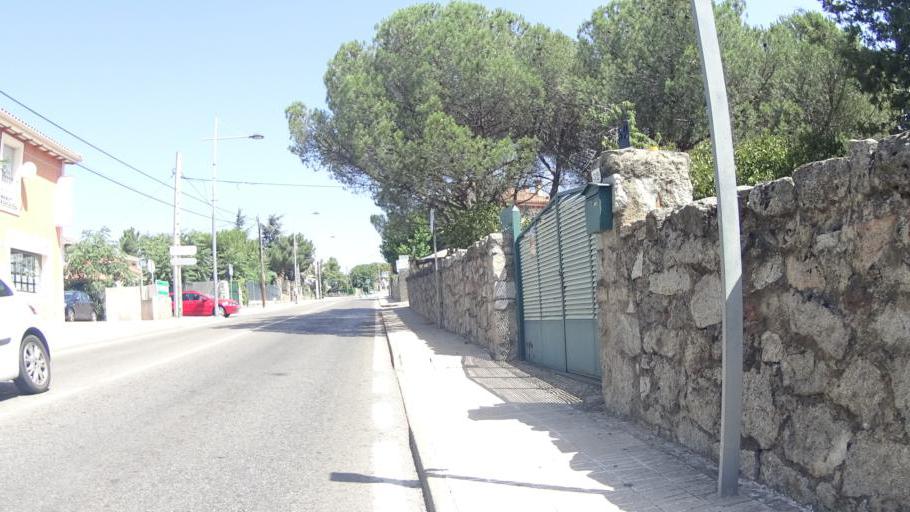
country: ES
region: Madrid
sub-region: Provincia de Madrid
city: Colmenarejo
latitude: 40.5646
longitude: -4.0138
